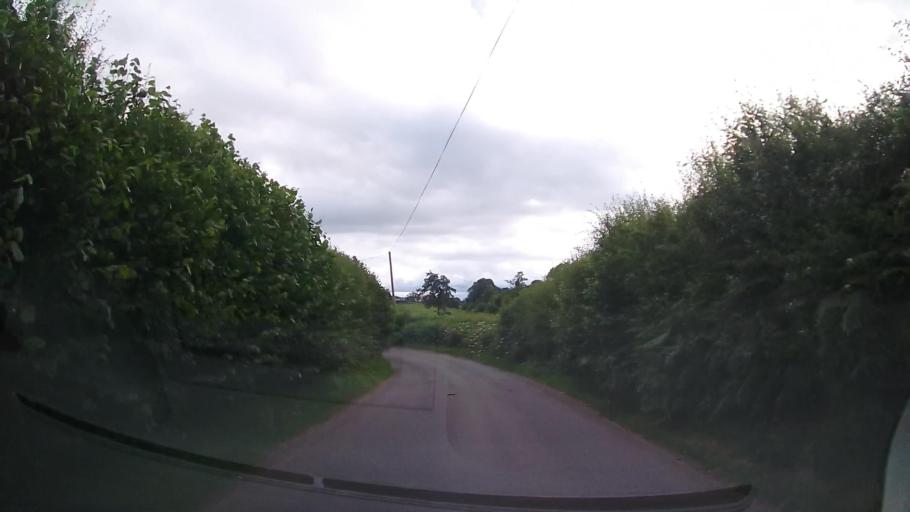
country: GB
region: England
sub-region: Shropshire
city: Whitchurch
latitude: 52.9324
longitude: -2.7248
